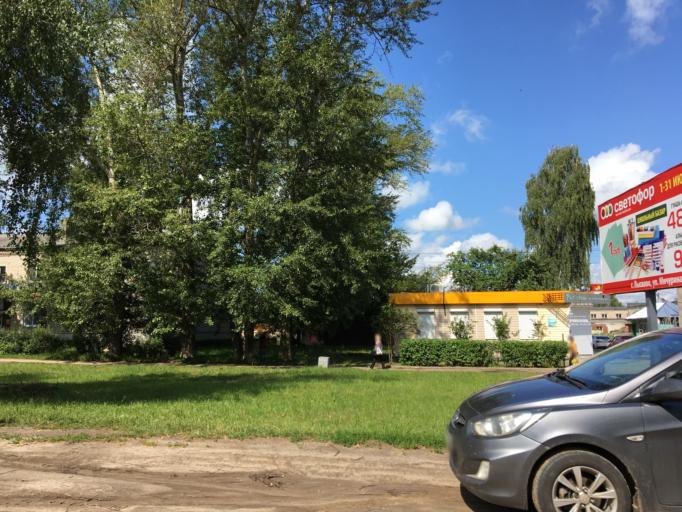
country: RU
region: Nizjnij Novgorod
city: Lyskovo
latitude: 56.0156
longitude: 45.0361
